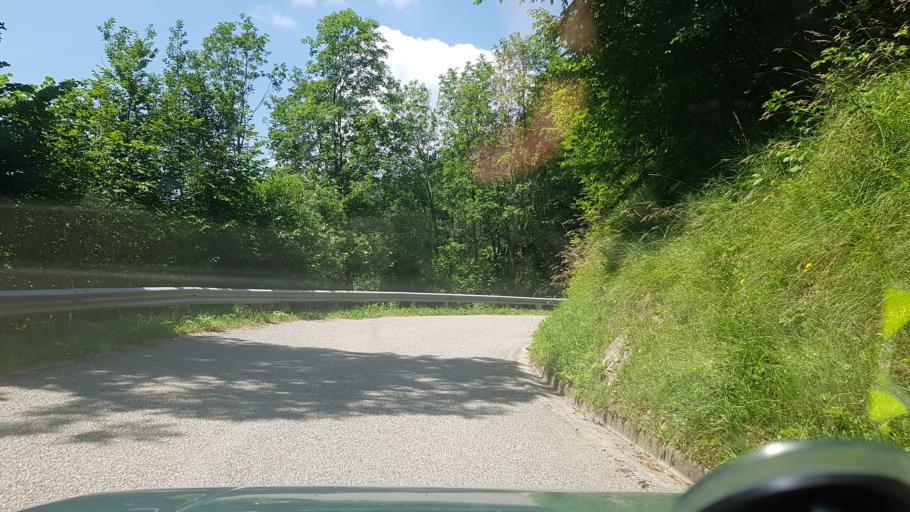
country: IT
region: Friuli Venezia Giulia
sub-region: Provincia di Udine
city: Lusevera
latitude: 46.2738
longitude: 13.3020
